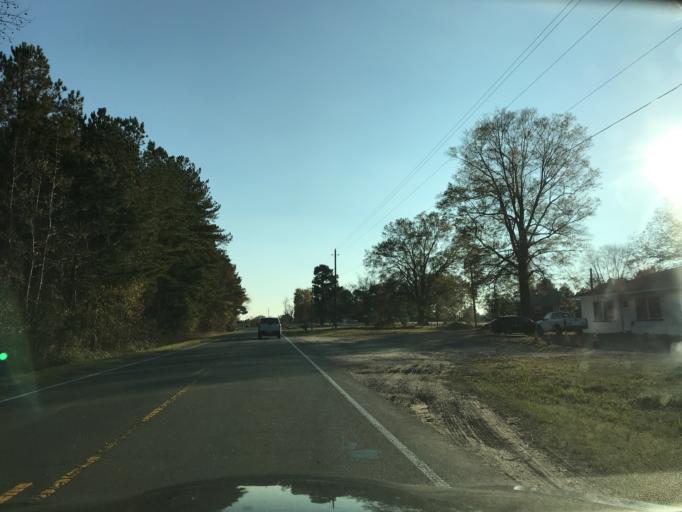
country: US
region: North Carolina
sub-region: Granville County
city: Creedmoor
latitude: 36.0578
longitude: -78.6971
